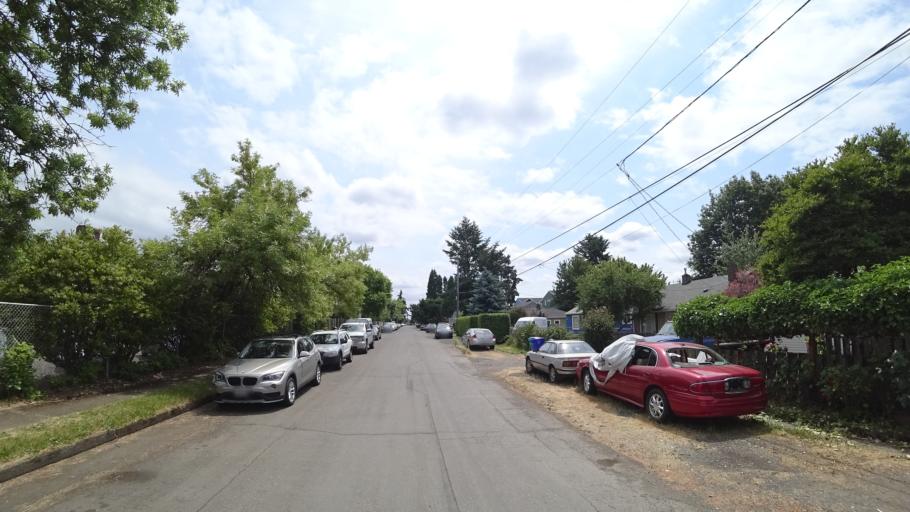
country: US
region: Oregon
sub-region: Multnomah County
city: Lents
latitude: 45.5072
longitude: -122.5757
